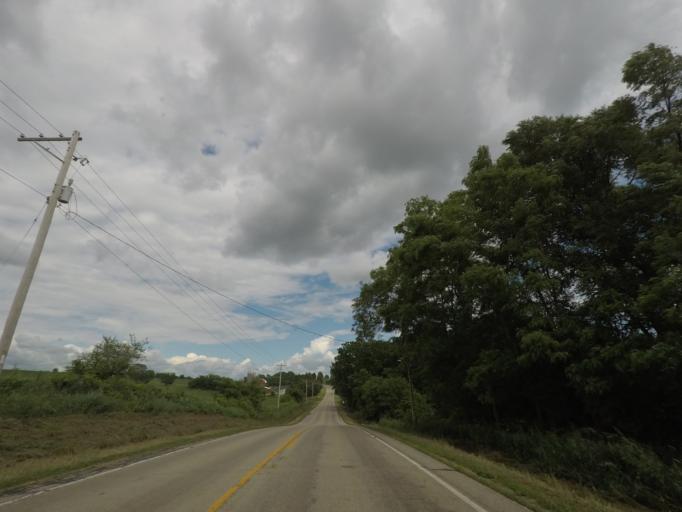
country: US
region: Wisconsin
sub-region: Green County
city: Brooklyn
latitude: 42.8280
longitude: -89.4218
